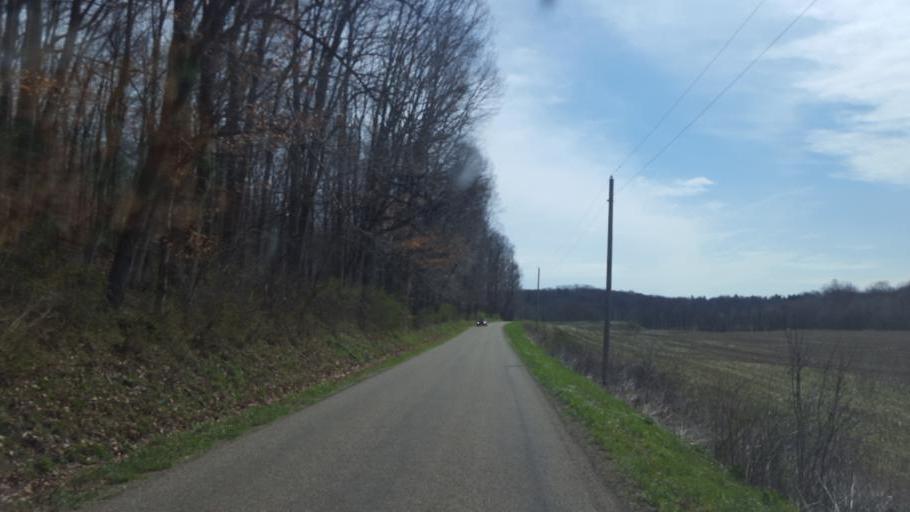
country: US
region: Ohio
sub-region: Knox County
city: Gambier
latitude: 40.3801
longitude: -82.4180
